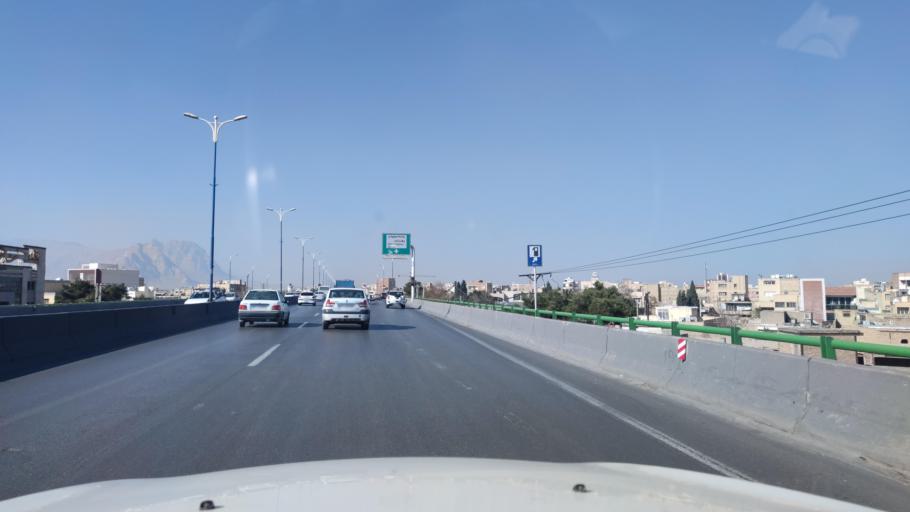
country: IR
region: Isfahan
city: Rehnan
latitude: 32.7006
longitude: 51.6168
